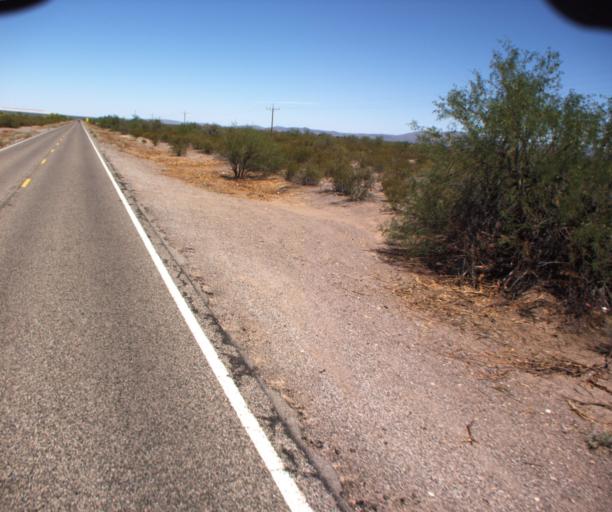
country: US
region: Arizona
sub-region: Pima County
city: Ajo
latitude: 32.2968
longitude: -112.7539
